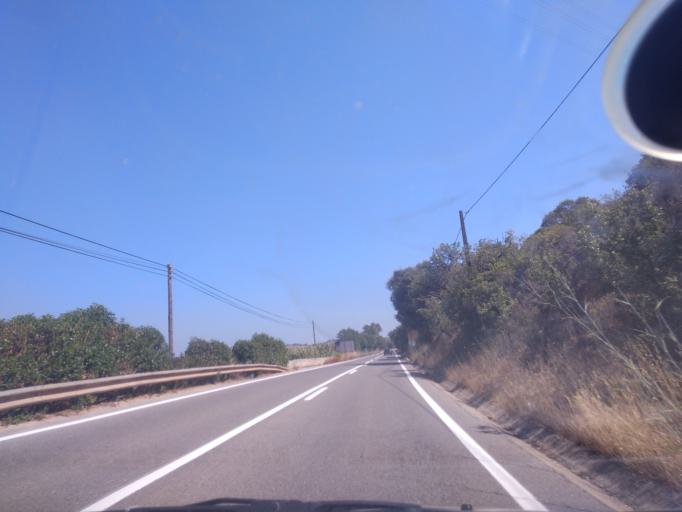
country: PT
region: Faro
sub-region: Lagos
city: Lagos
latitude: 37.1345
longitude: -8.6986
